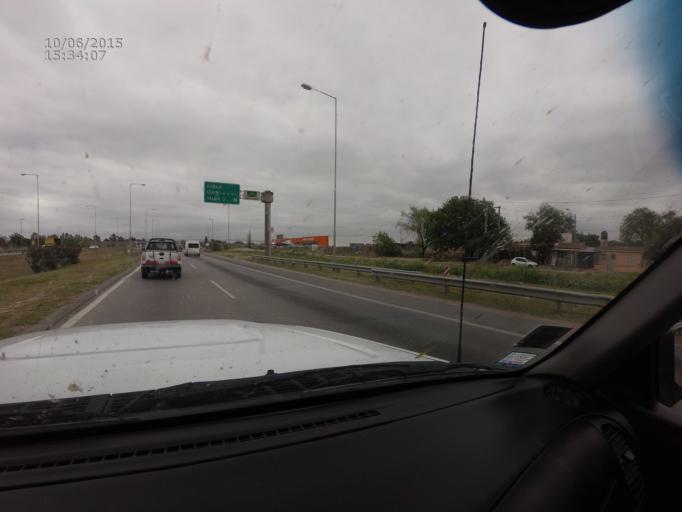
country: AR
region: Cordoba
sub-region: Departamento de Capital
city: Cordoba
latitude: -31.3584
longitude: -64.1712
